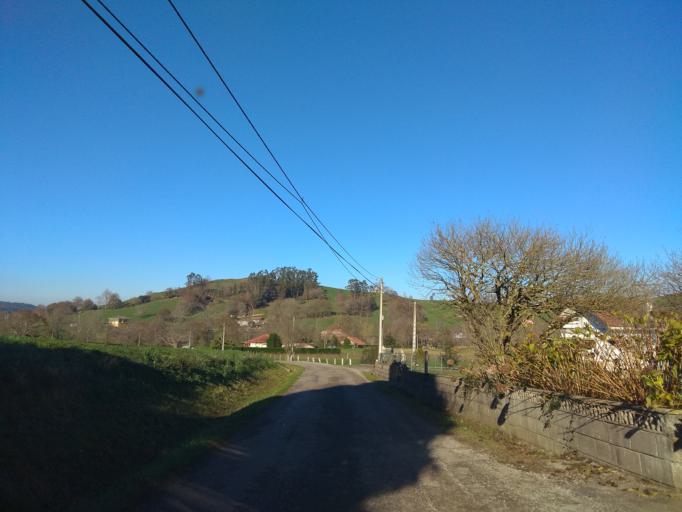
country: ES
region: Cantabria
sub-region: Provincia de Cantabria
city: Entrambasaguas
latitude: 43.3692
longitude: -3.6616
